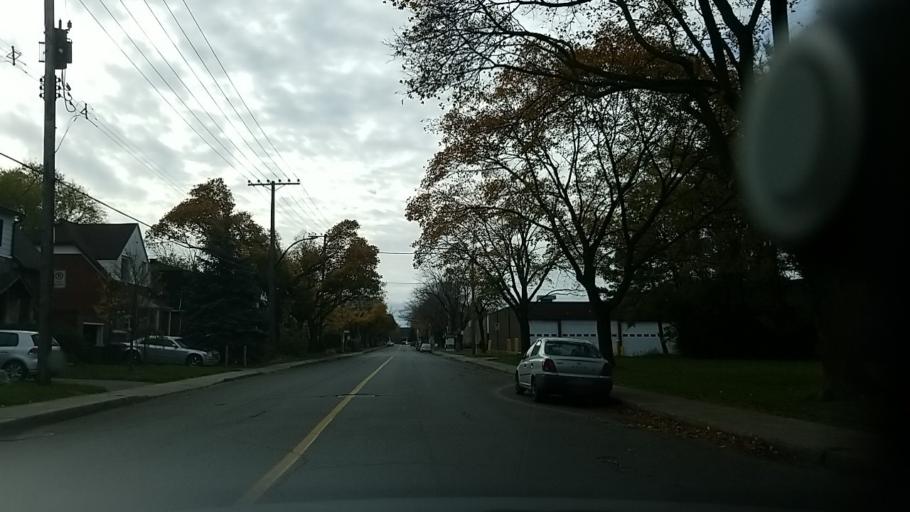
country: CA
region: Quebec
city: Saint-Laurent
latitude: 45.5124
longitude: -73.6655
